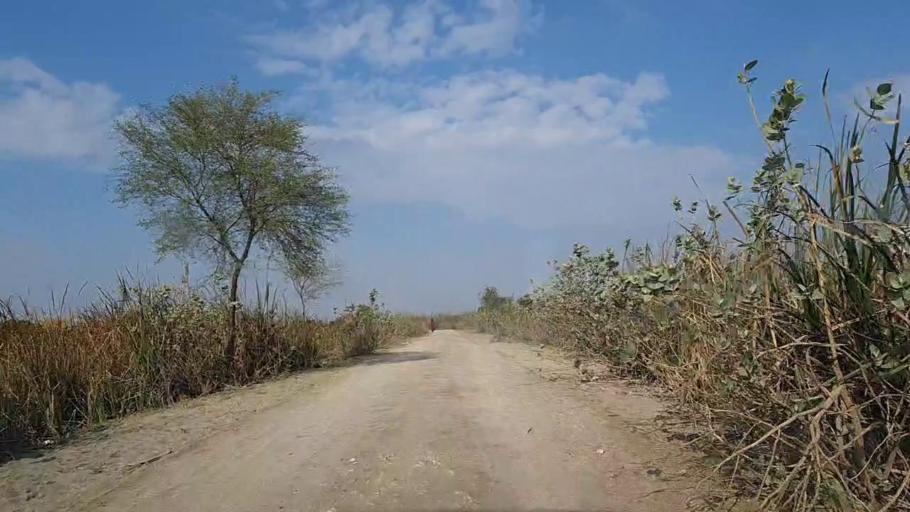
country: PK
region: Sindh
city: Sanghar
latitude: 26.2678
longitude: 69.0118
